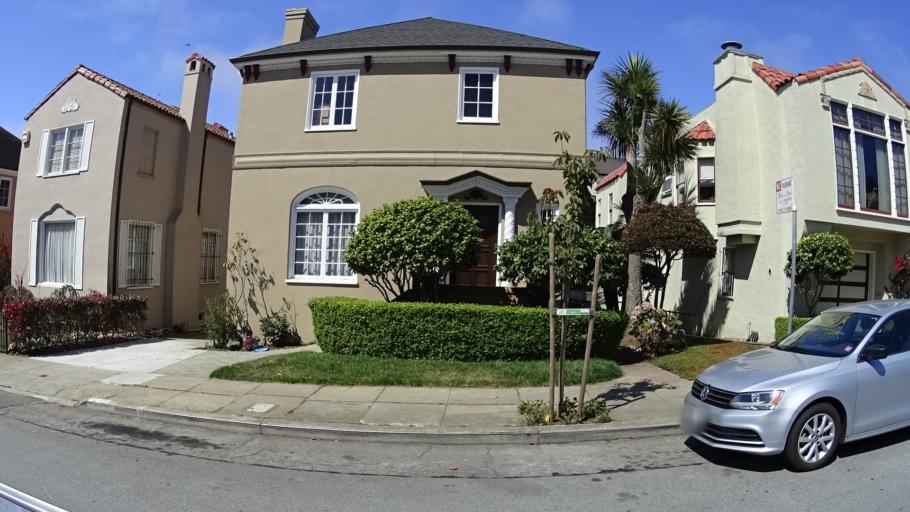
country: US
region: California
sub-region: San Mateo County
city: Daly City
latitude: 37.7297
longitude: -122.4647
